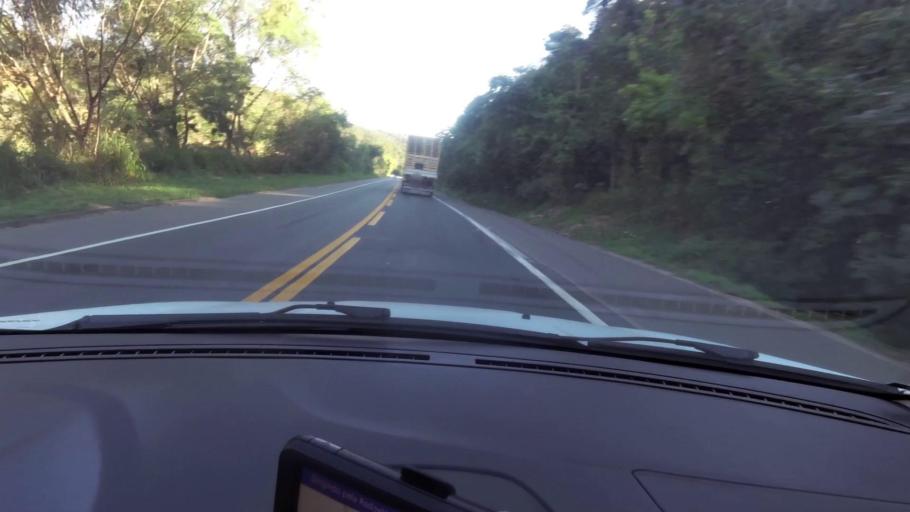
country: BR
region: Espirito Santo
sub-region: Alfredo Chaves
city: Alfredo Chaves
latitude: -20.6613
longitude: -40.6510
